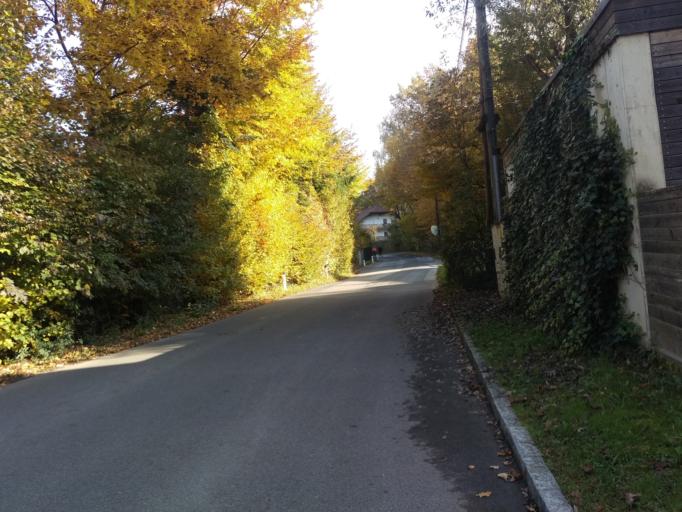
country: AT
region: Styria
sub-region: Graz Stadt
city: Mariatrost
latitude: 47.1047
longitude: 15.4967
